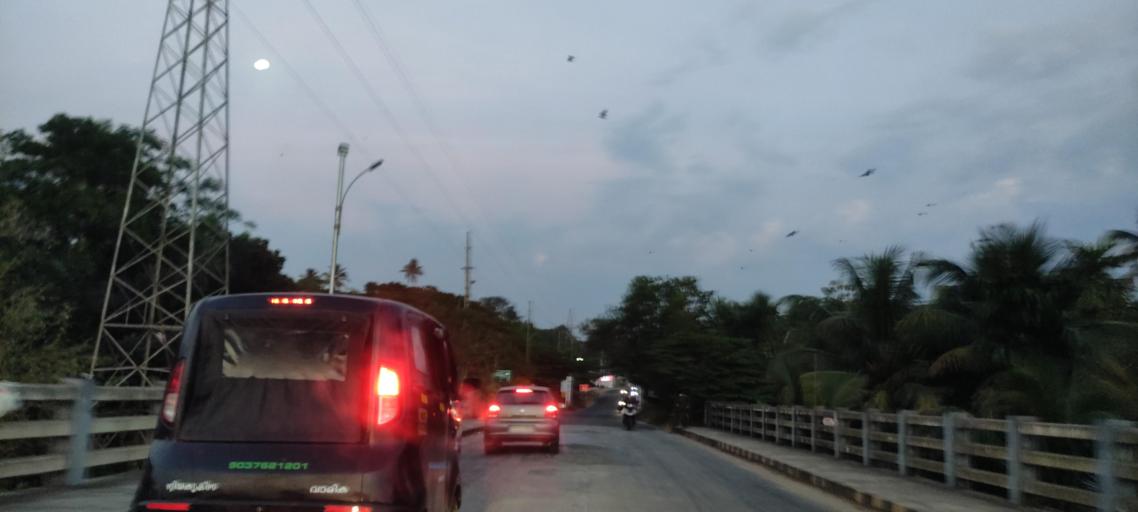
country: IN
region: Kerala
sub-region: Alappuzha
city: Kutiatodu
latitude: 9.7753
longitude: 76.3360
